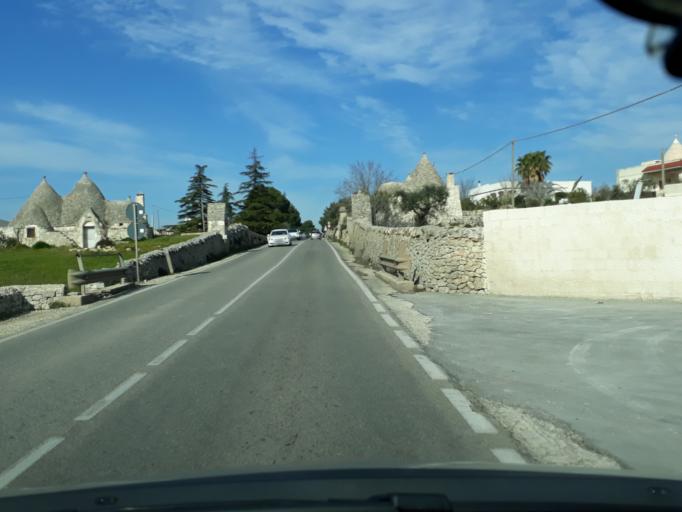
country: IT
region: Apulia
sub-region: Provincia di Bari
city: Locorotondo
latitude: 40.7385
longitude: 17.3325
